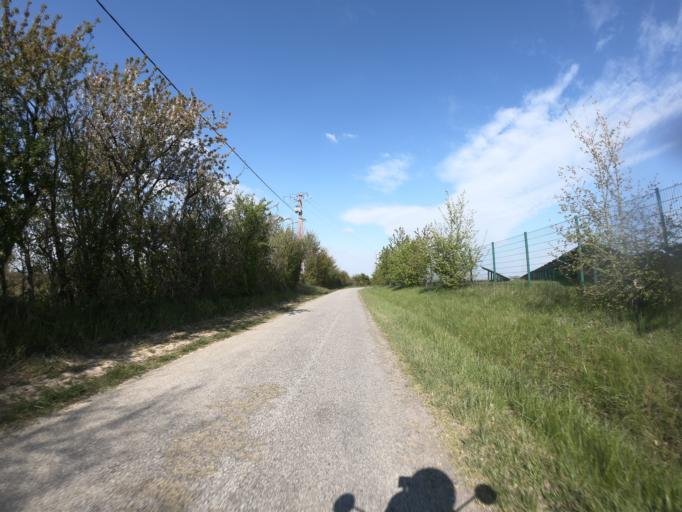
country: FR
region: Midi-Pyrenees
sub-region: Departement de l'Ariege
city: La Tour-du-Crieu
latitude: 43.1073
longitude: 1.6927
